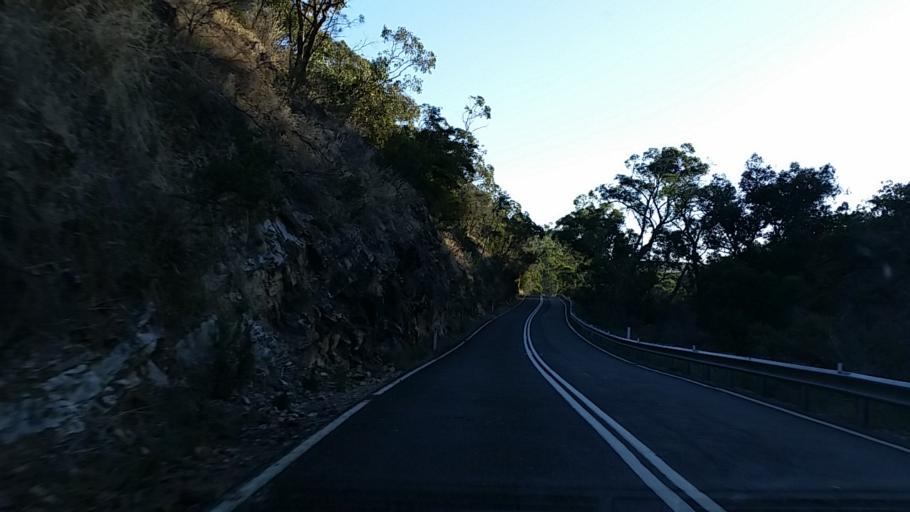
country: AU
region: South Australia
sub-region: Adelaide Hills
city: Gumeracha
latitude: -34.8410
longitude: 138.8426
